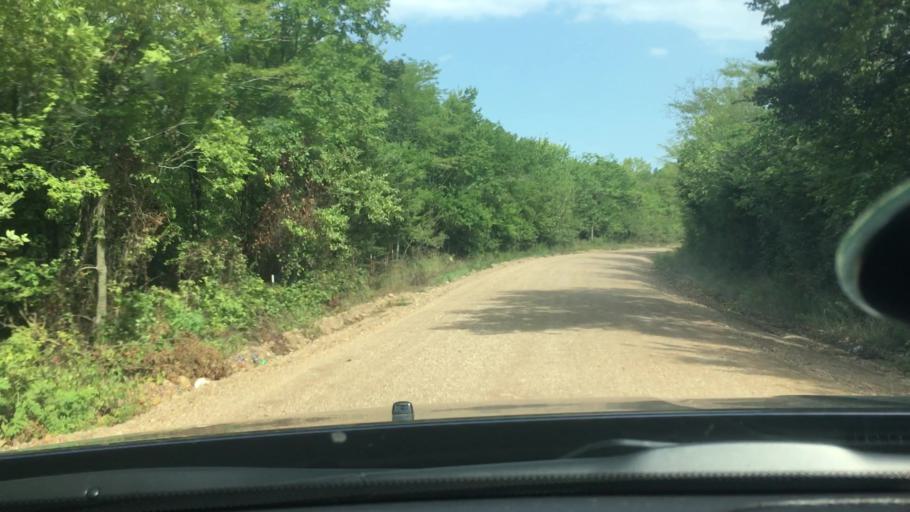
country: US
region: Oklahoma
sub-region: Atoka County
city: Atoka
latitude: 34.4419
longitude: -96.0669
